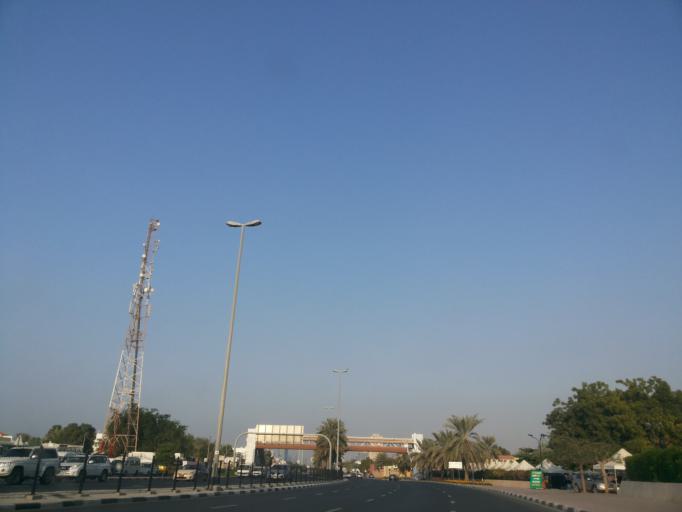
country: AE
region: Ash Shariqah
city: Sharjah
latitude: 25.2841
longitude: 55.3395
